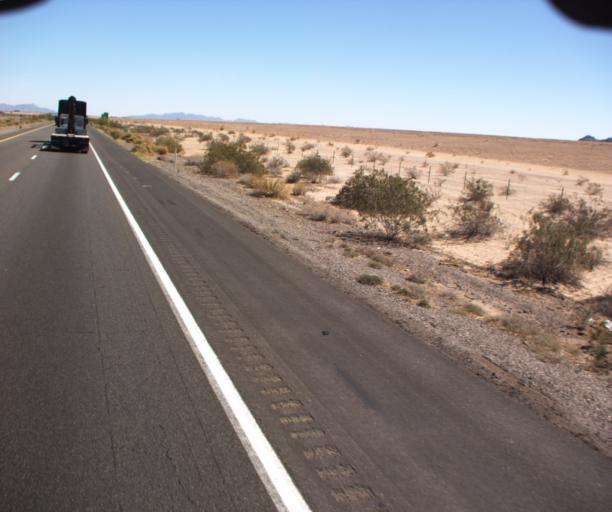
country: US
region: Arizona
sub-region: Yuma County
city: Wellton
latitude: 32.6778
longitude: -114.0392
